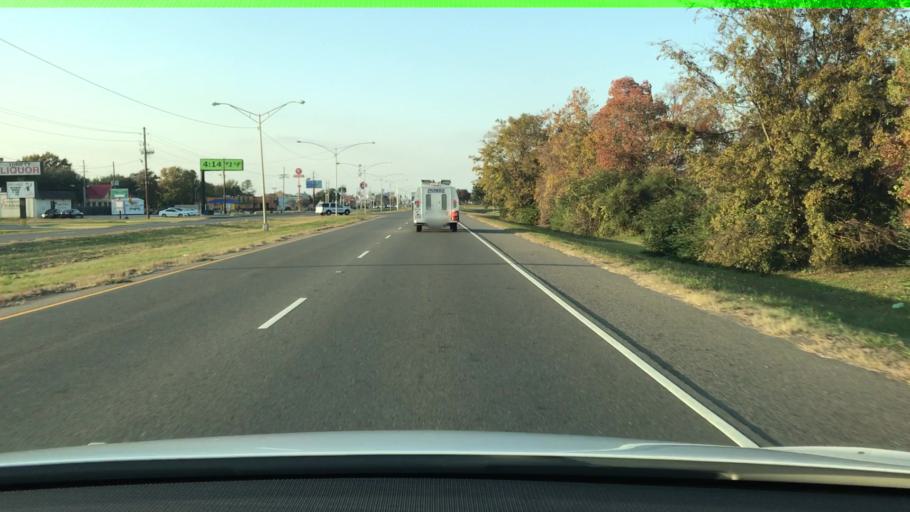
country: US
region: Louisiana
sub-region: Bossier Parish
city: Bossier City
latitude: 32.4229
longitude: -93.7065
